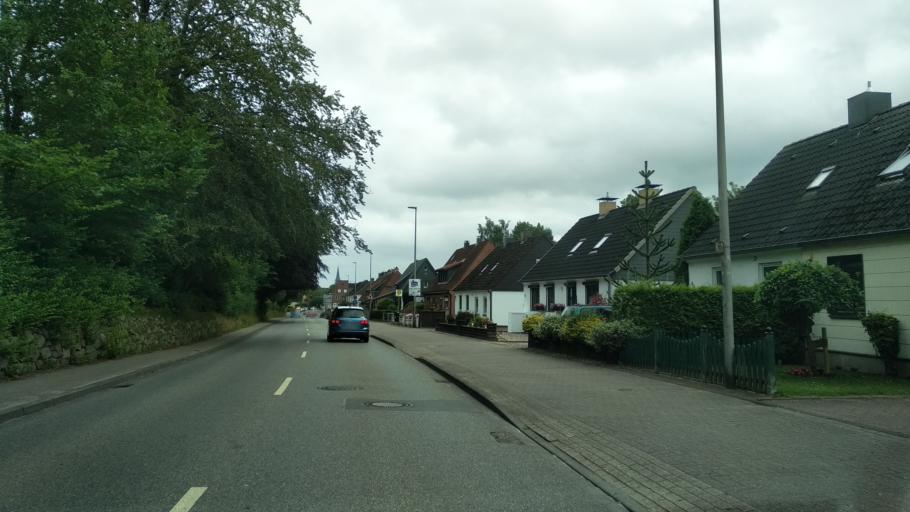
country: DE
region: Schleswig-Holstein
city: Schleswig
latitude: 54.5272
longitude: 9.5590
